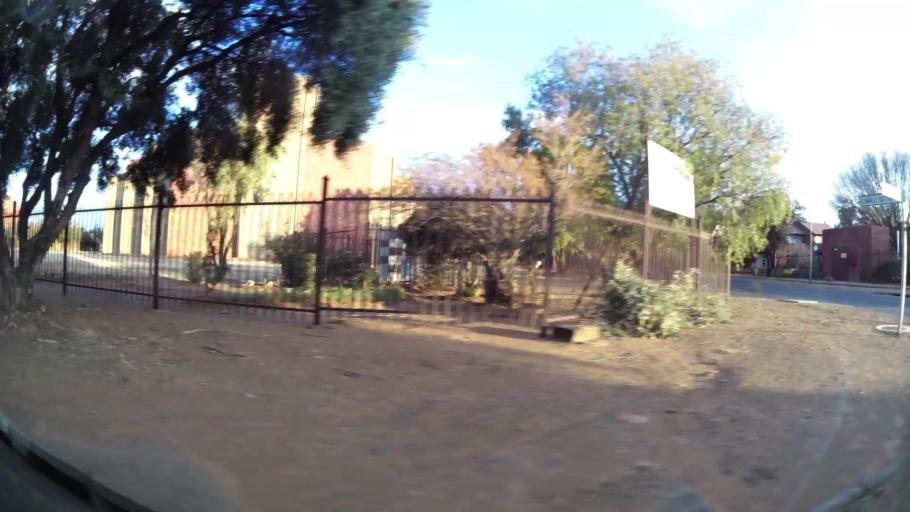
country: ZA
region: Orange Free State
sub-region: Mangaung Metropolitan Municipality
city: Bloemfontein
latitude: -29.1427
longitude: 26.1773
